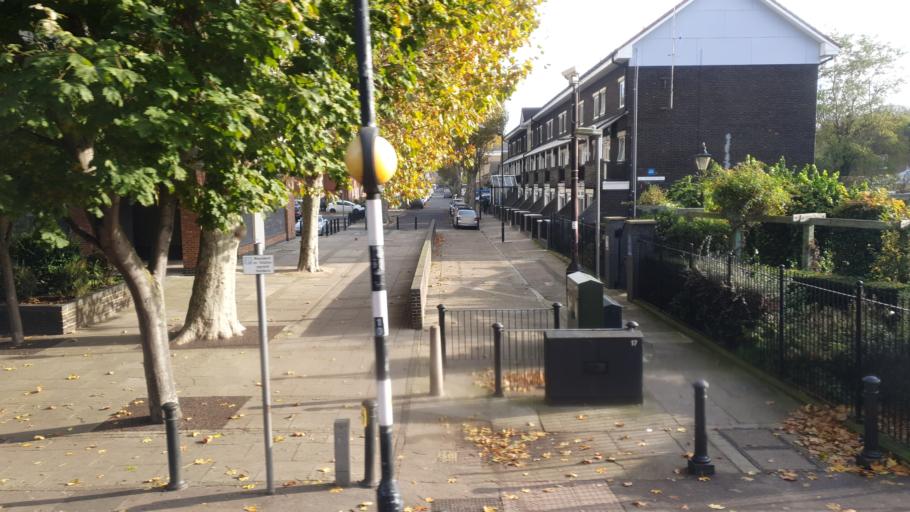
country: GB
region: England
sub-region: Greater London
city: Poplar
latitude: 51.4968
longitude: -0.0258
